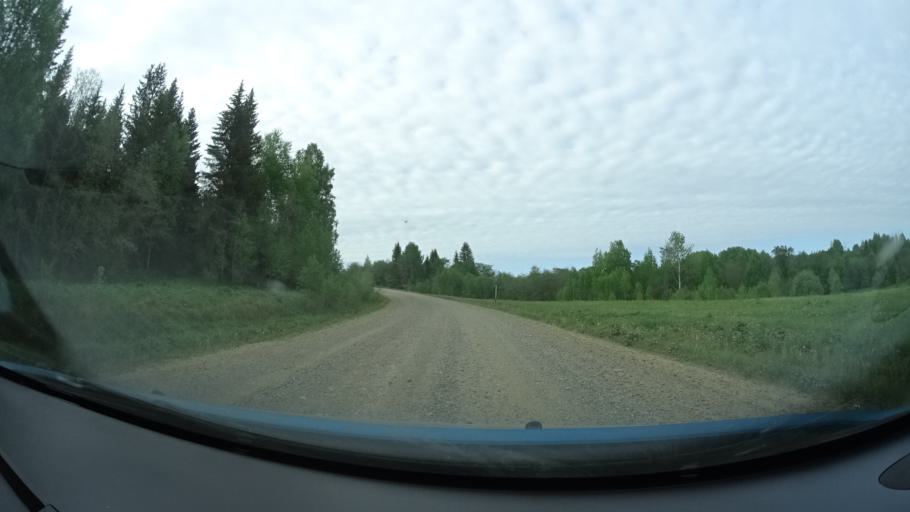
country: RU
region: Perm
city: Kuyeda
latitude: 56.6570
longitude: 55.6918
